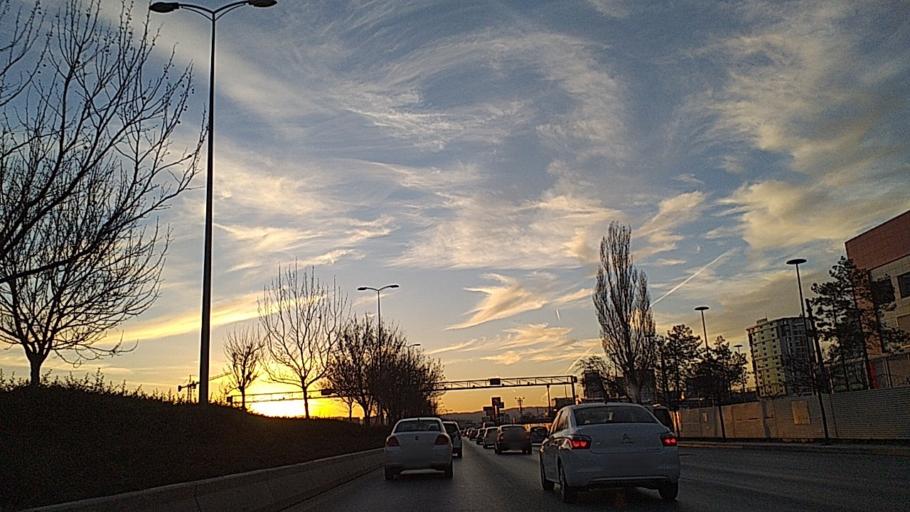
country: TR
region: Ankara
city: Etimesgut
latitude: 39.9635
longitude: 32.6506
